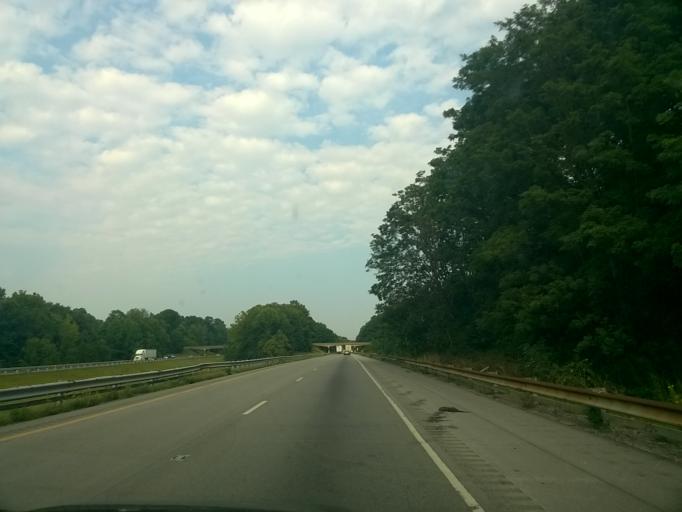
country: US
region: Indiana
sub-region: Putnam County
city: Cloverdale
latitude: 39.5170
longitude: -86.9096
